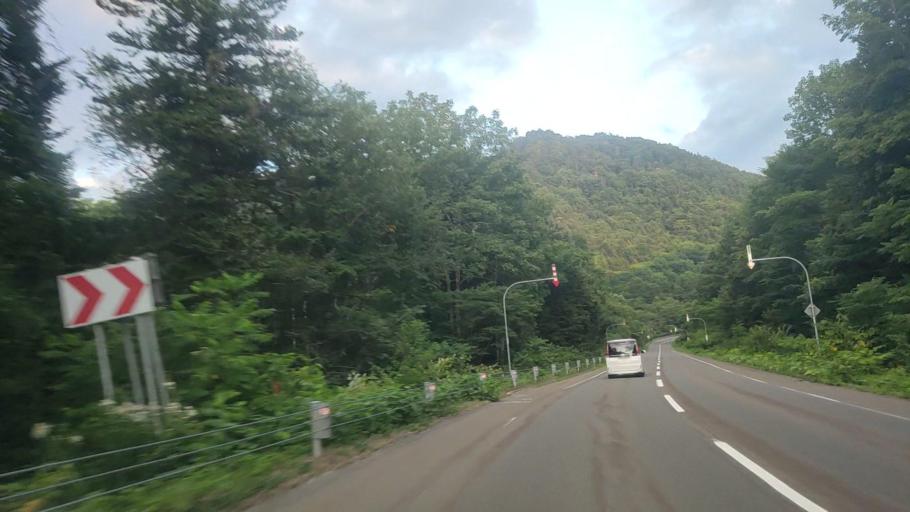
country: JP
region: Hokkaido
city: Shimo-furano
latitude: 43.3638
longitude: 142.2378
